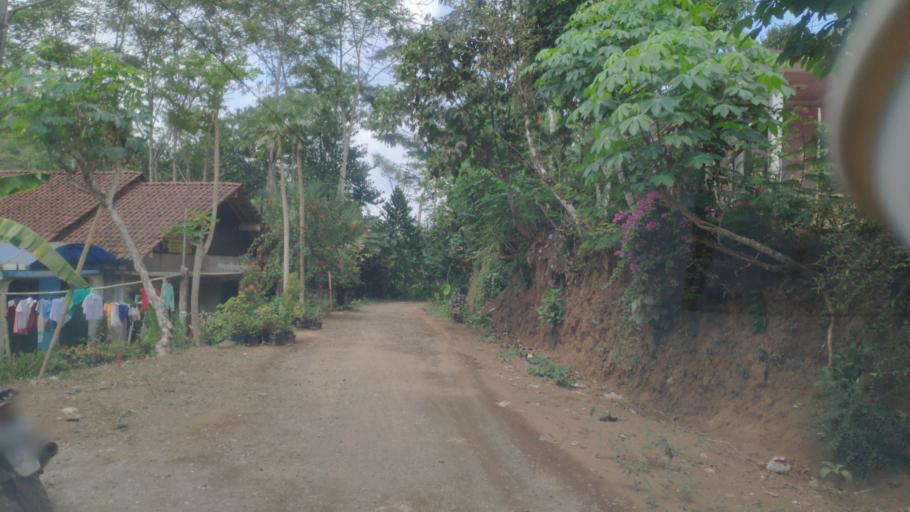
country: ID
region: Central Java
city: Purbalingga
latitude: -7.3446
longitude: 109.6198
